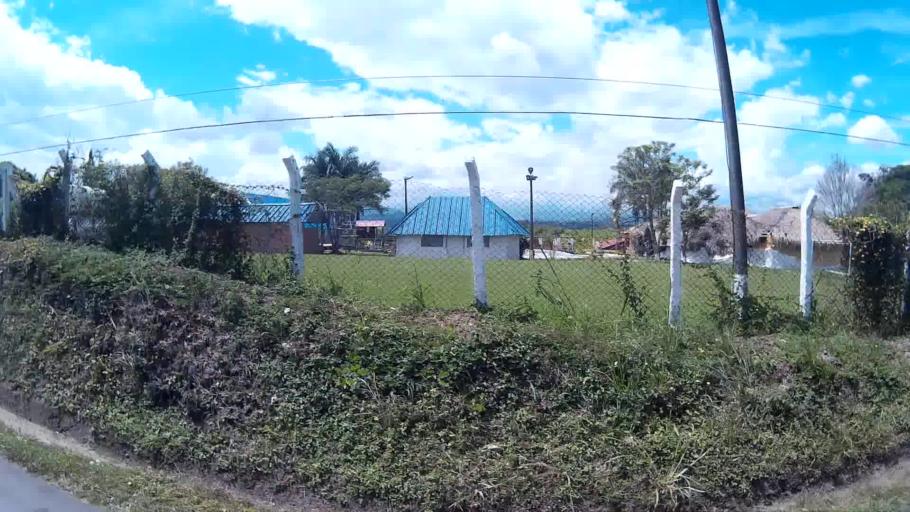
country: CO
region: Valle del Cauca
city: Cartago
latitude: 4.8123
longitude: -75.8404
